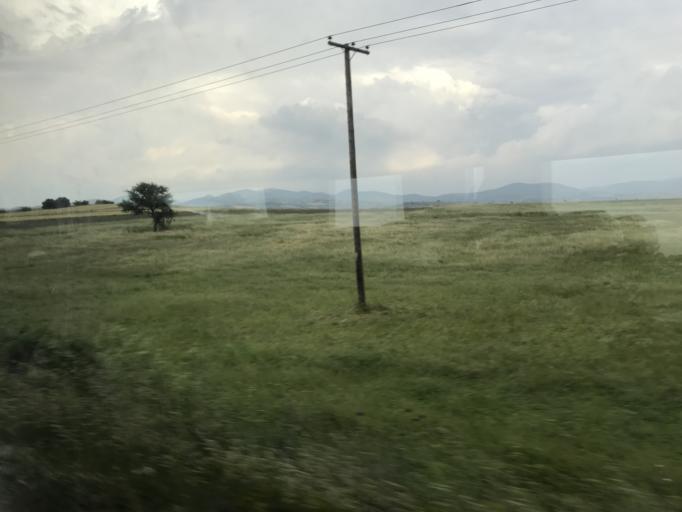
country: GR
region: East Macedonia and Thrace
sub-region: Nomos Rodopis
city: Sapes
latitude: 40.9890
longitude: 25.6559
